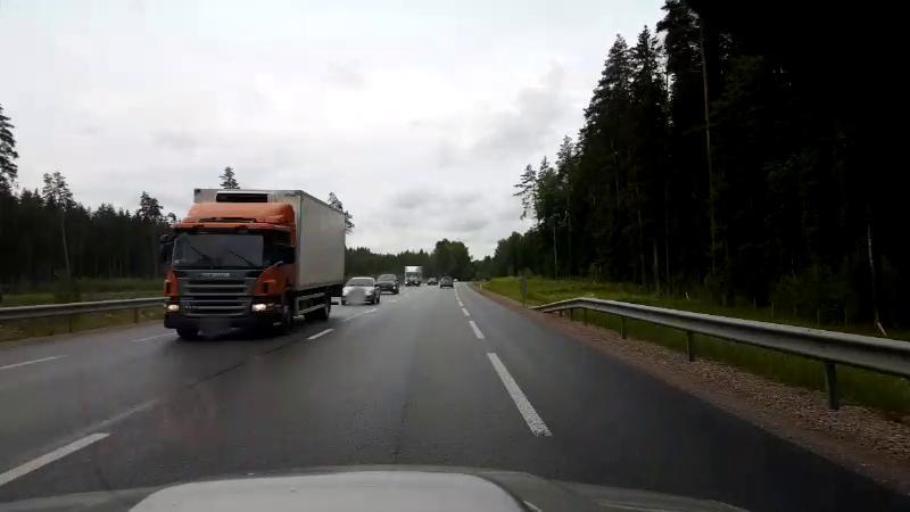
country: LV
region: Kekava
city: Kekava
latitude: 56.7216
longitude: 24.2527
